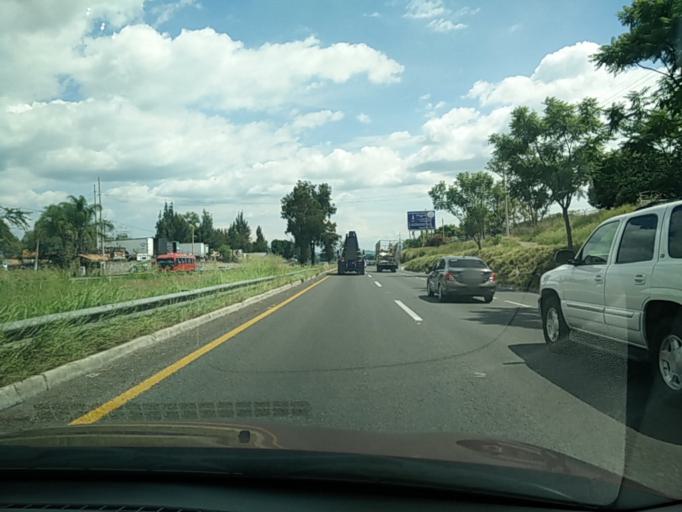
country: MX
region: Jalisco
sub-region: Tlajomulco de Zuniga
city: Rancho Alegre [Fraccionamiento]
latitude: 20.4734
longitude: -103.2626
